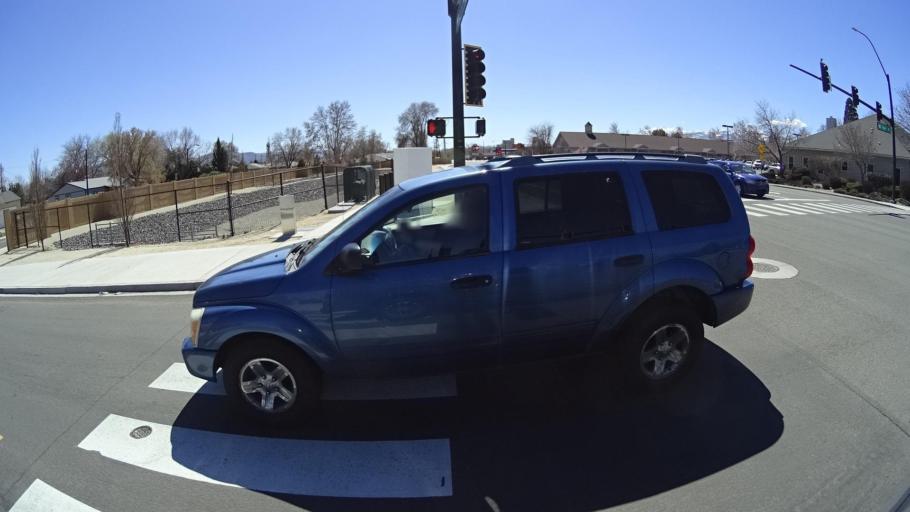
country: US
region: Nevada
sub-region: Washoe County
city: Sparks
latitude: 39.5528
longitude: -119.7523
